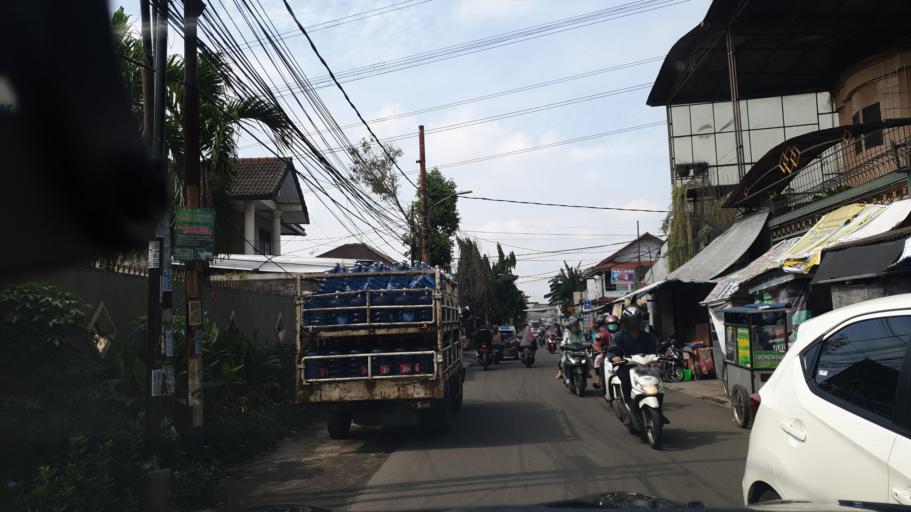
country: ID
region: West Java
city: Pamulang
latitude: -6.3145
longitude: 106.7543
